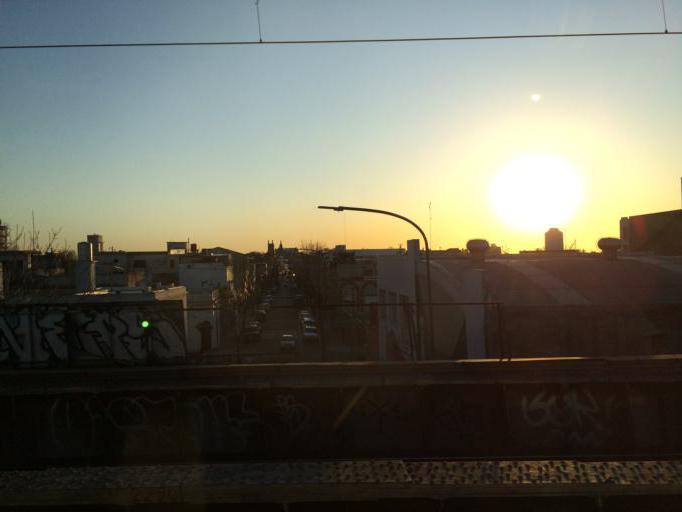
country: AR
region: Buenos Aires
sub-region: Partido de Avellaneda
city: Avellaneda
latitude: -34.6486
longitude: -58.3802
